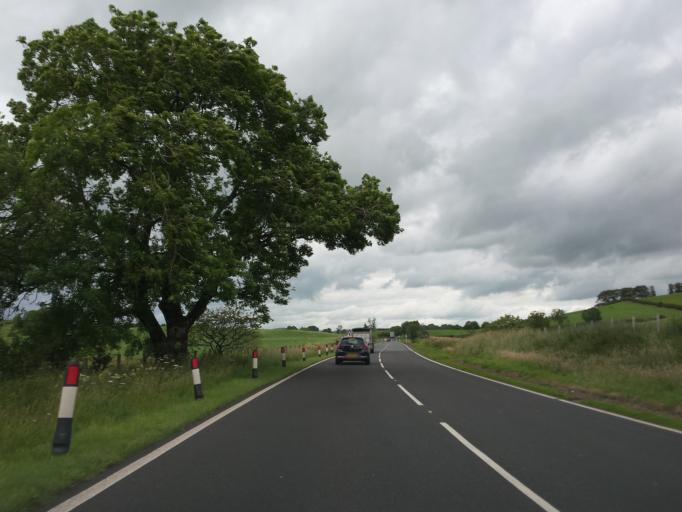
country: GB
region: Scotland
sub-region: Dumfries and Galloway
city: Castle Douglas
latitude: 54.9953
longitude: -3.8841
